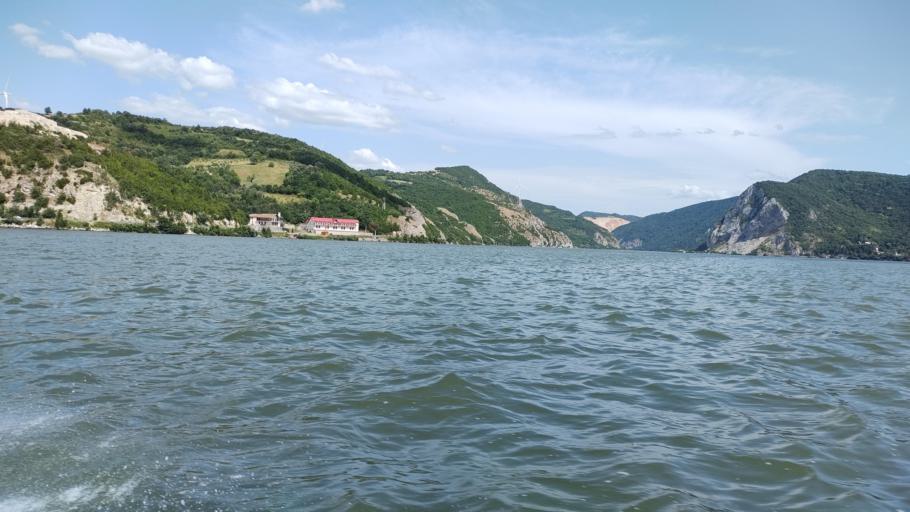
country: RO
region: Caras-Severin
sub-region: Comuna Pescari
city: Coronini
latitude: 44.6718
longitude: 21.6750
